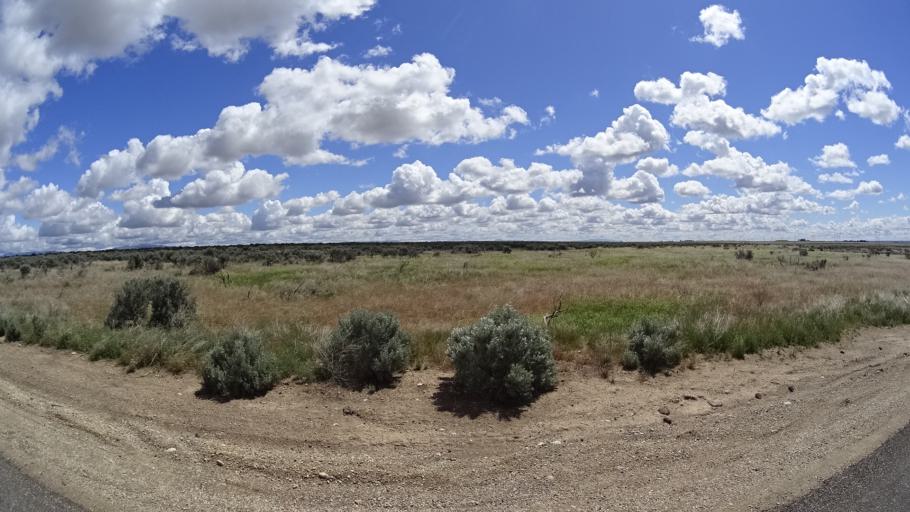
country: US
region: Idaho
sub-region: Ada County
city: Garden City
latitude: 43.4804
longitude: -116.2743
